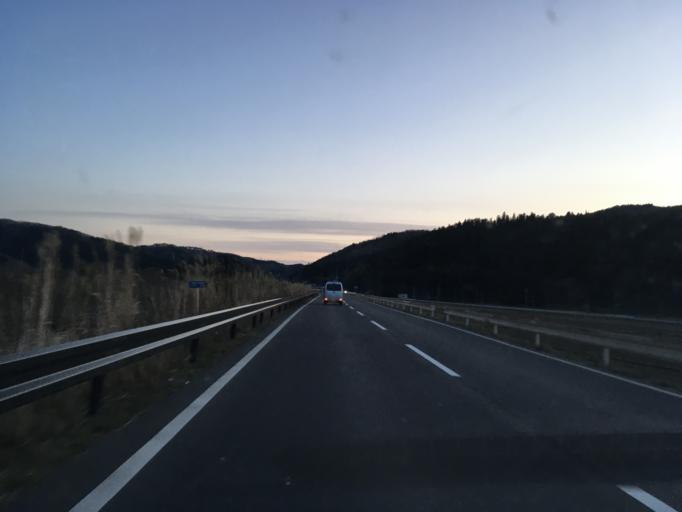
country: JP
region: Iwate
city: Ichinoseki
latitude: 38.7540
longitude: 141.3250
